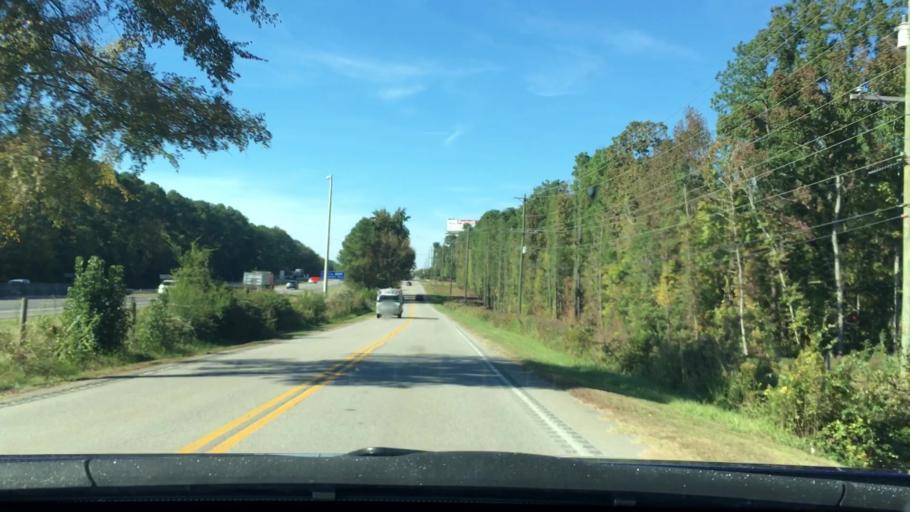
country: US
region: South Carolina
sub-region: Lexington County
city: Irmo
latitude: 34.1053
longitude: -81.1809
